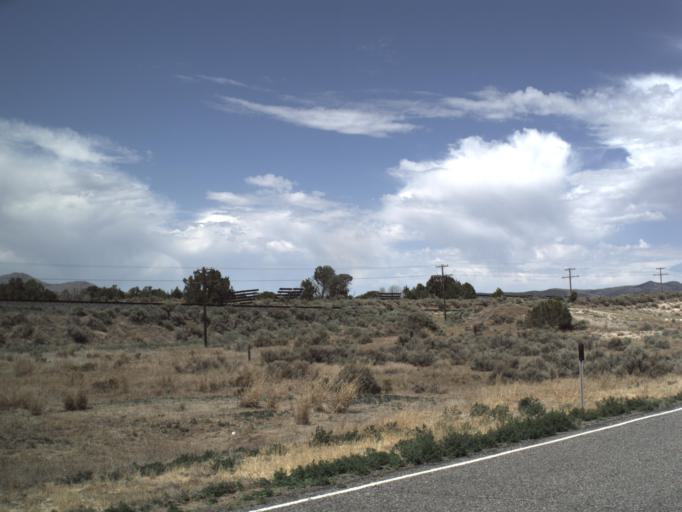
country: US
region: Utah
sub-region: Utah County
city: Genola
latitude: 39.9393
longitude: -112.1839
